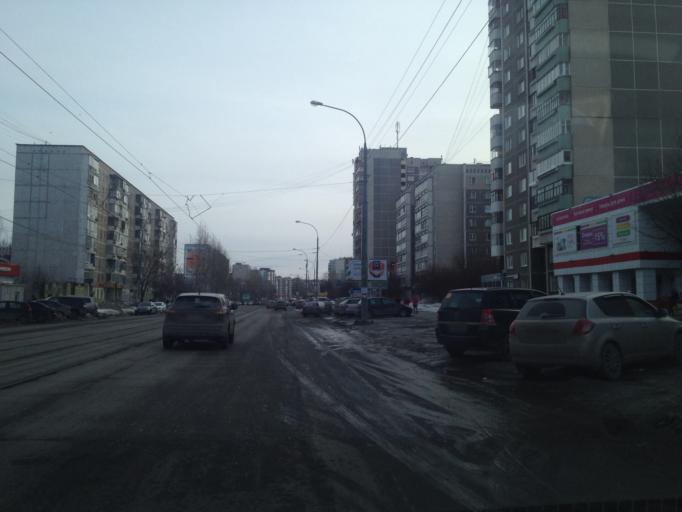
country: RU
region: Sverdlovsk
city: Shirokaya Rechka
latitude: 56.8334
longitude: 60.5452
